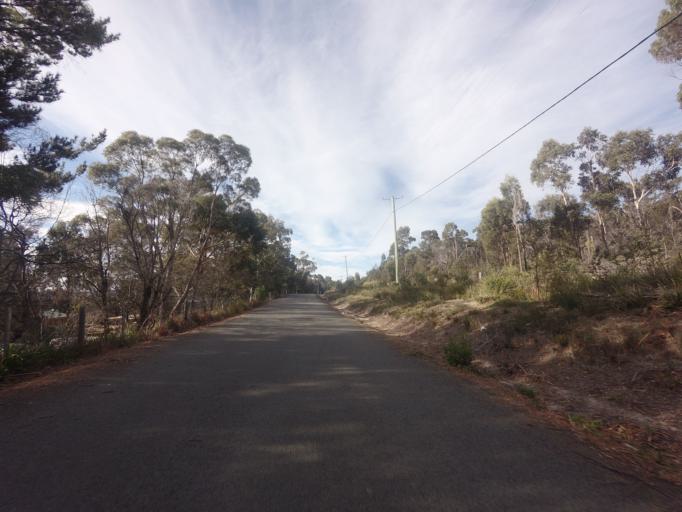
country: AU
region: Tasmania
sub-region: Sorell
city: Sorell
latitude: -42.9612
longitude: 147.8379
